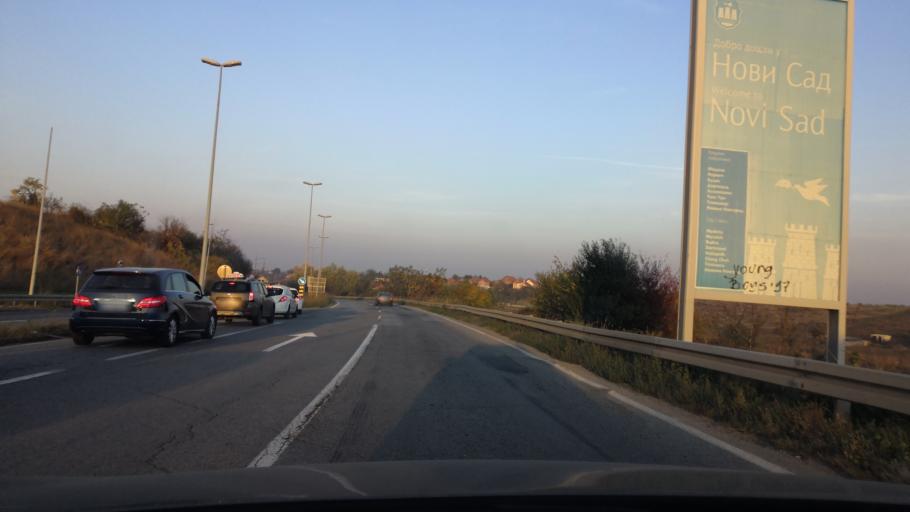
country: RS
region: Autonomna Pokrajina Vojvodina
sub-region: Juznobacki Okrug
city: Petrovaradin
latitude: 45.2240
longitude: 19.8755
